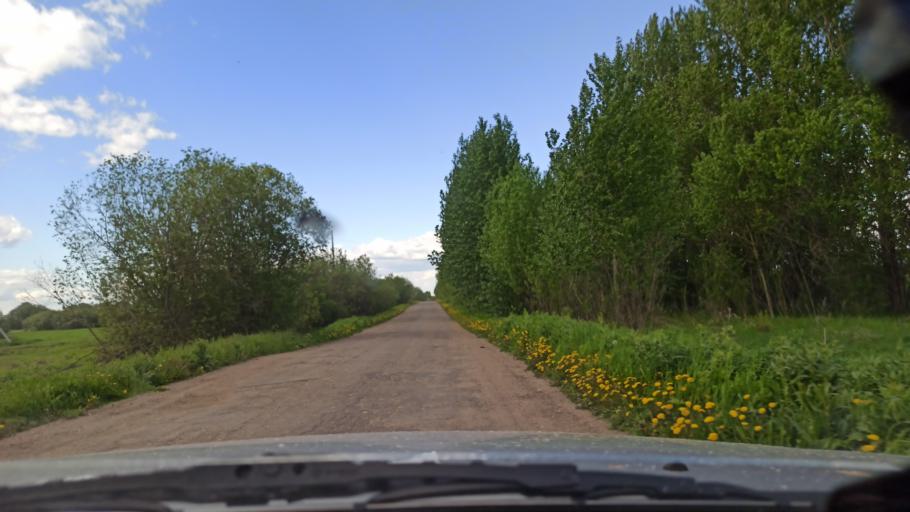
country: RU
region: Vologda
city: Vologda
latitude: 59.3328
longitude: 39.8387
